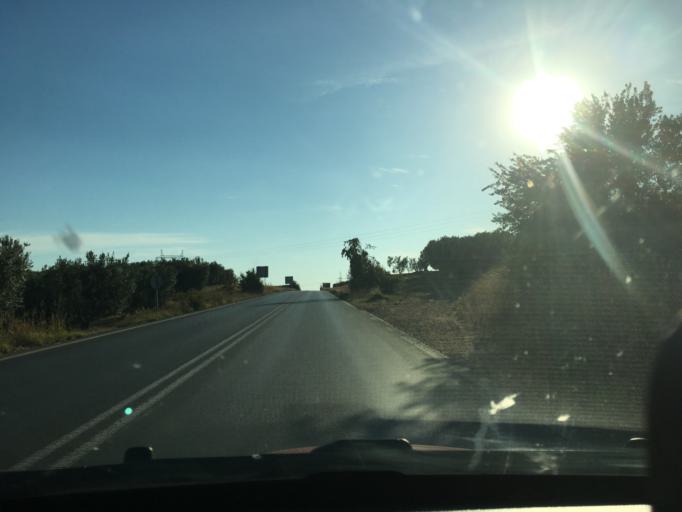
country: GR
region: Central Macedonia
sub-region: Nomos Chalkidikis
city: Olynthos
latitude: 40.2724
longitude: 23.3431
